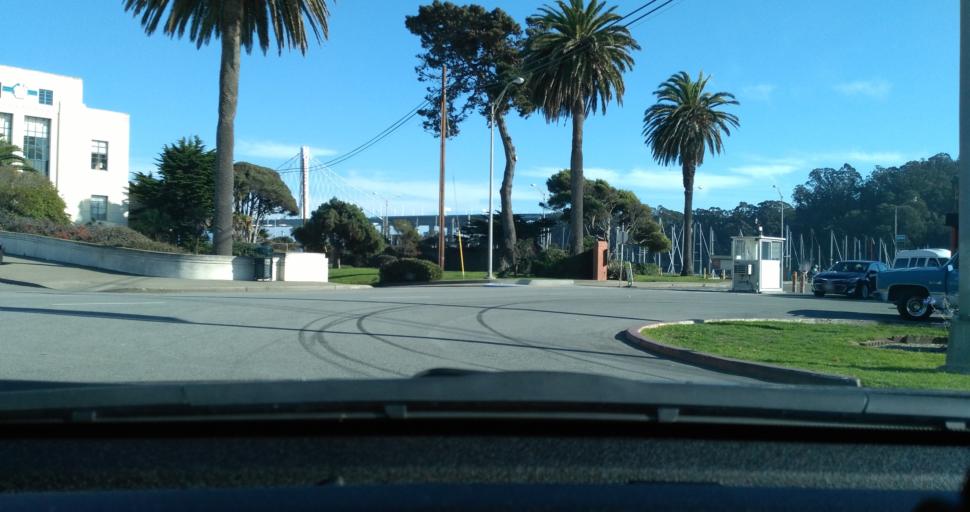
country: US
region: California
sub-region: San Francisco County
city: San Francisco
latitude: 37.8166
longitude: -122.3720
